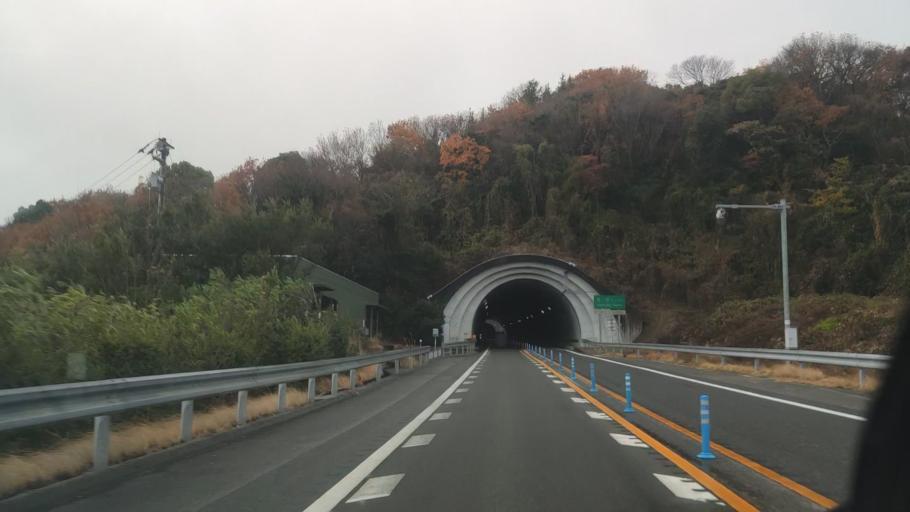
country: JP
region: Tokushima
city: Kamojimacho-jogejima
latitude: 34.1154
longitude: 134.3243
